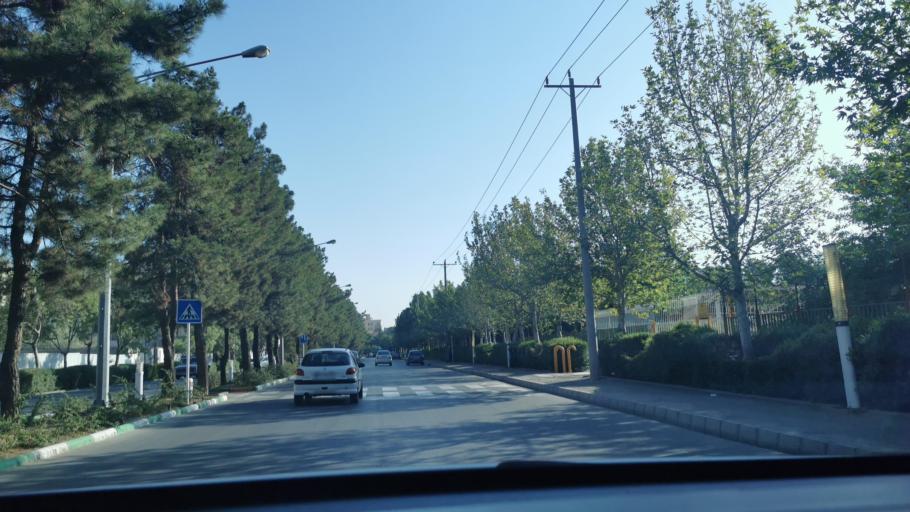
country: IR
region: Razavi Khorasan
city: Mashhad
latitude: 36.3170
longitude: 59.5267
